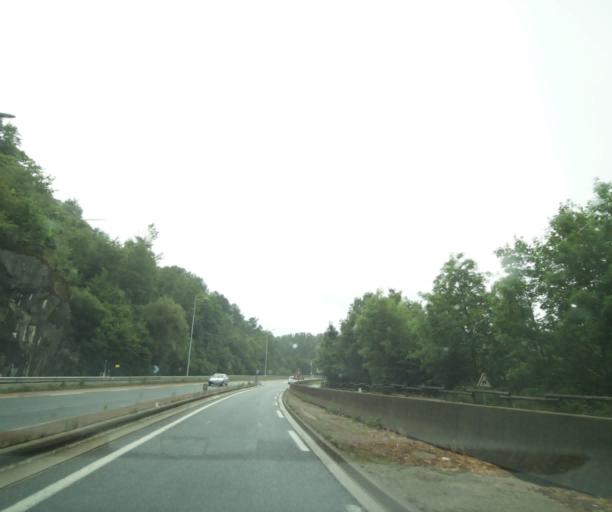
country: FR
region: Midi-Pyrenees
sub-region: Departement de l'Aveyron
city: Olemps
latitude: 44.3500
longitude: 2.5544
